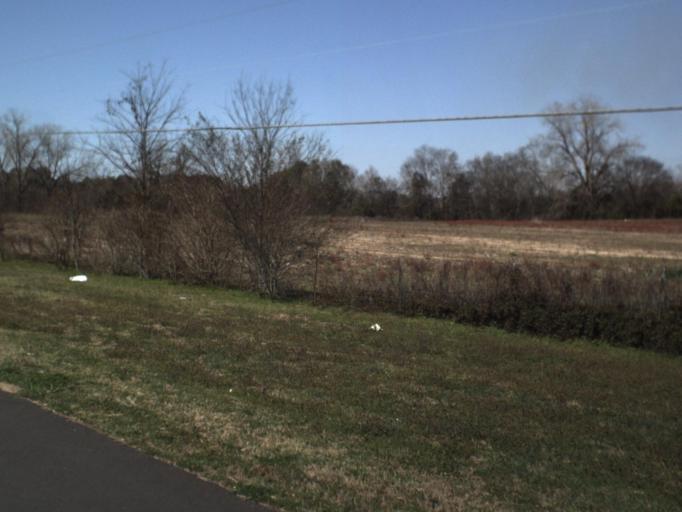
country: US
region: Florida
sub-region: Jackson County
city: Malone
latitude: 30.8700
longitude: -85.1447
